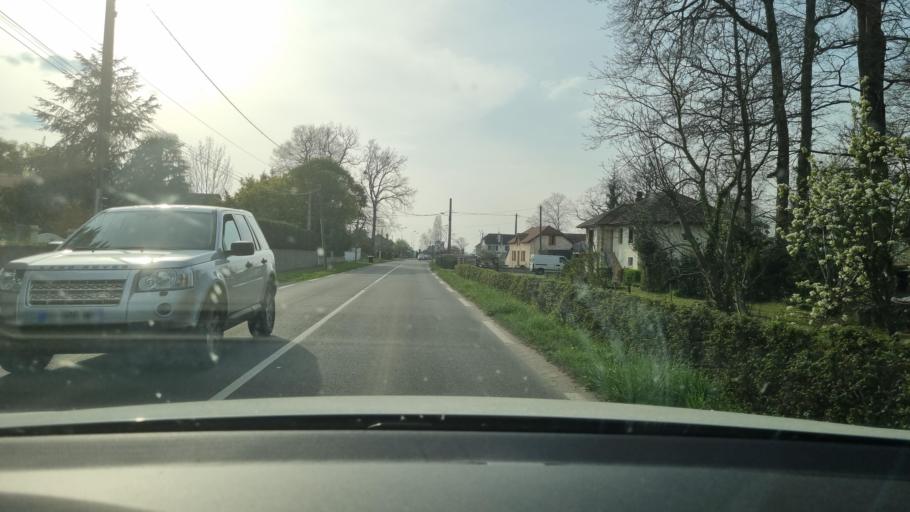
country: FR
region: Aquitaine
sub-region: Departement des Pyrenees-Atlantiques
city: Morlaas
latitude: 43.3589
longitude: -0.2419
